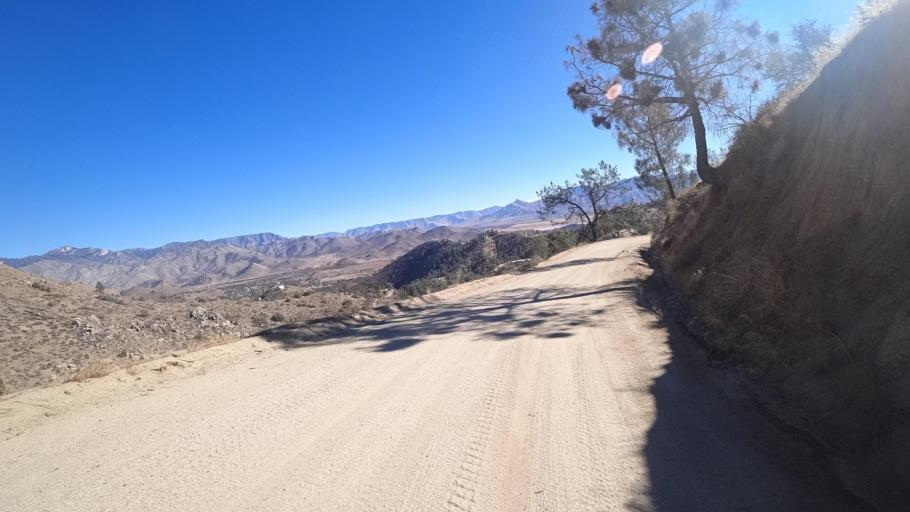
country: US
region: California
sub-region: Kern County
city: Wofford Heights
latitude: 35.7029
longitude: -118.4866
